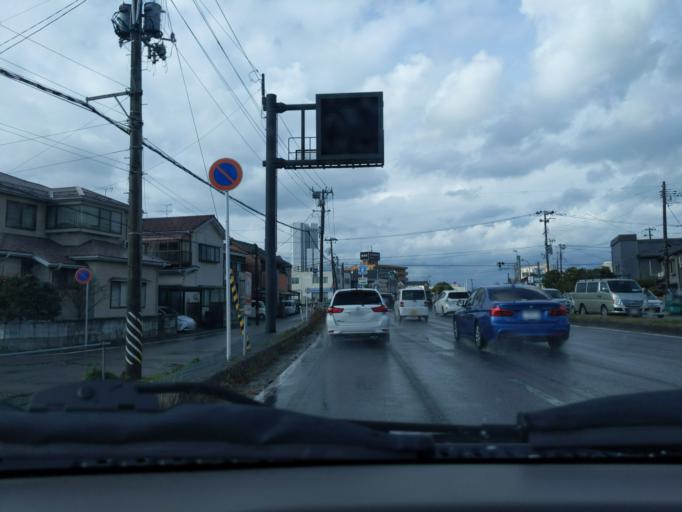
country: JP
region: Niigata
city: Niigata-shi
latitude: 37.9197
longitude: 139.0685
